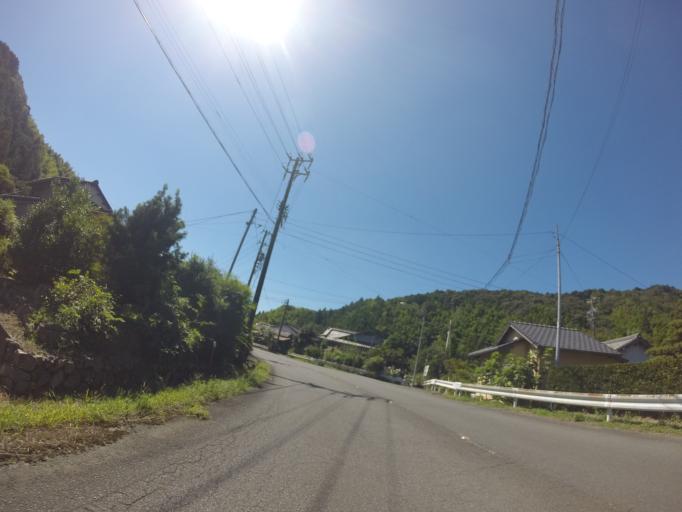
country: JP
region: Shizuoka
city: Fujieda
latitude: 34.9360
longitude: 138.2050
